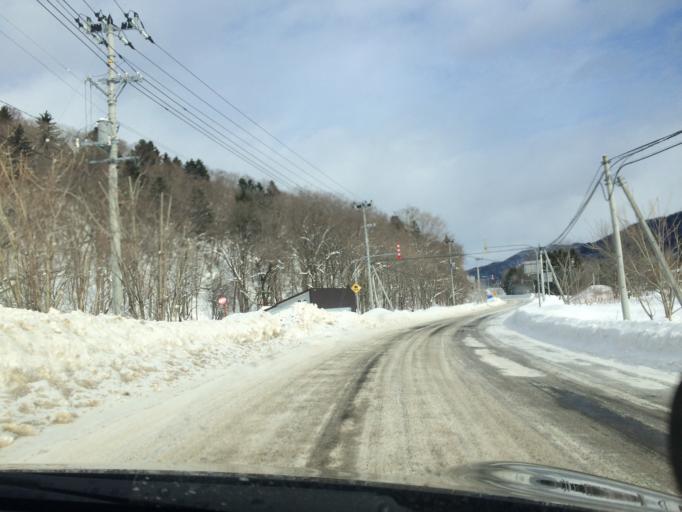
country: JP
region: Hokkaido
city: Shimo-furano
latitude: 43.0073
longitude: 142.4078
